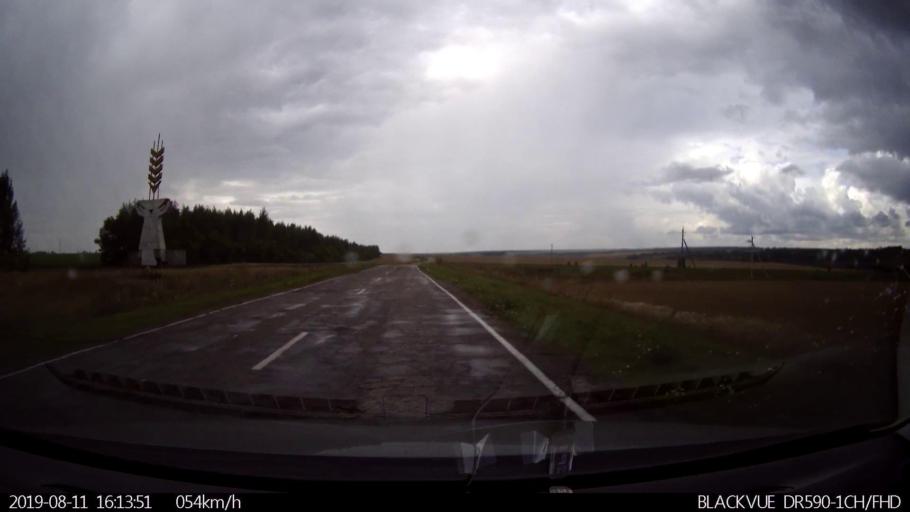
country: RU
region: Ulyanovsk
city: Ignatovka
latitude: 54.0234
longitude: 47.6356
